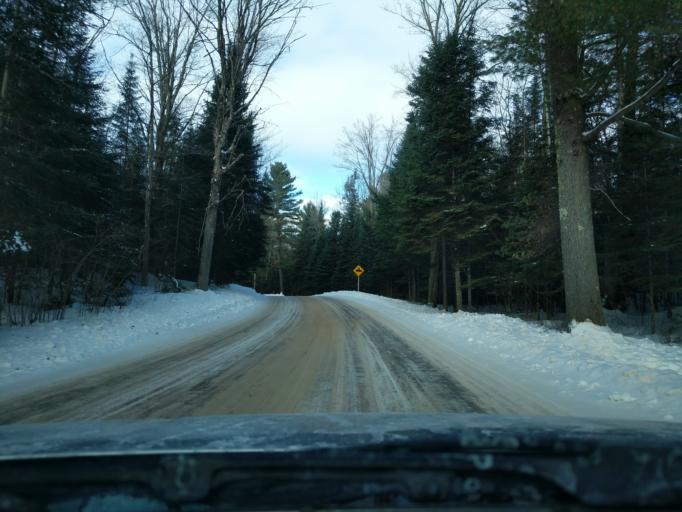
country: US
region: Wisconsin
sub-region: Vilas County
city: Eagle River
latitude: 45.8058
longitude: -89.0705
